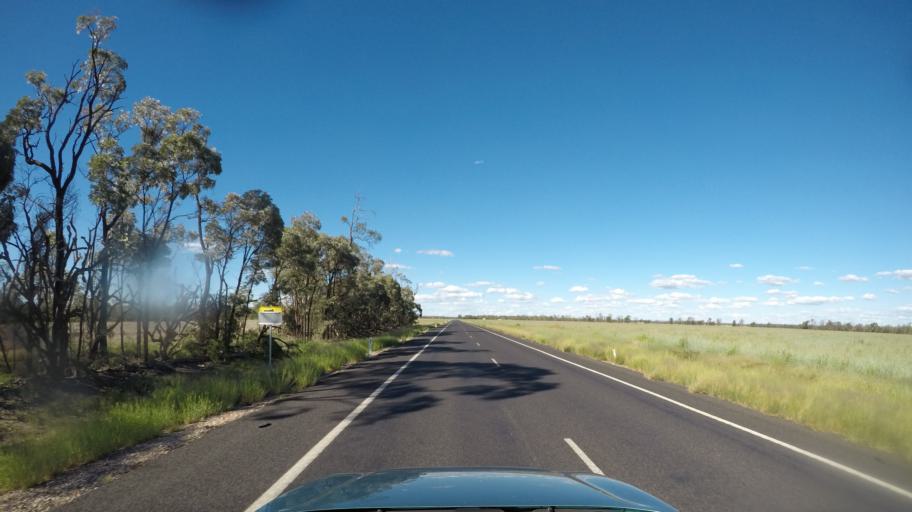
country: AU
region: Queensland
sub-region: Goondiwindi
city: Goondiwindi
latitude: -28.1284
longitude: 150.7018
